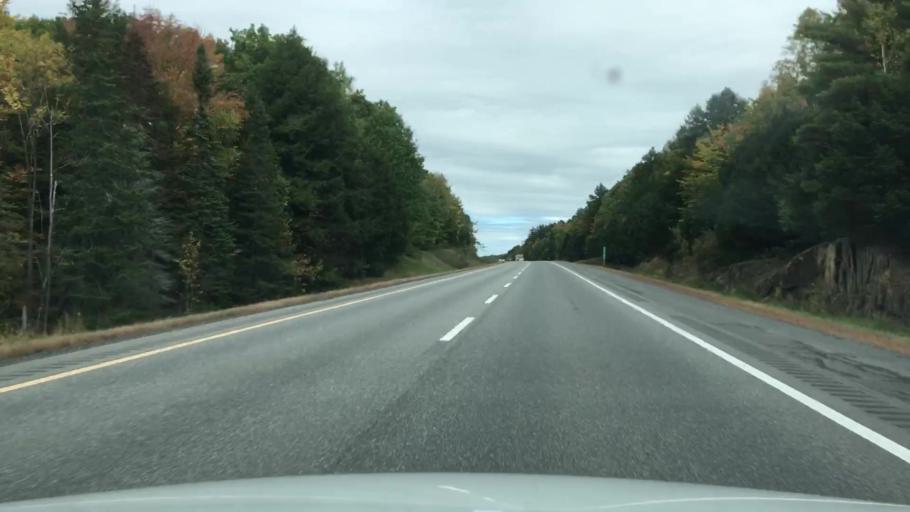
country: US
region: Maine
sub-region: Kennebec County
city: Sidney
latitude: 44.3936
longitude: -69.7567
